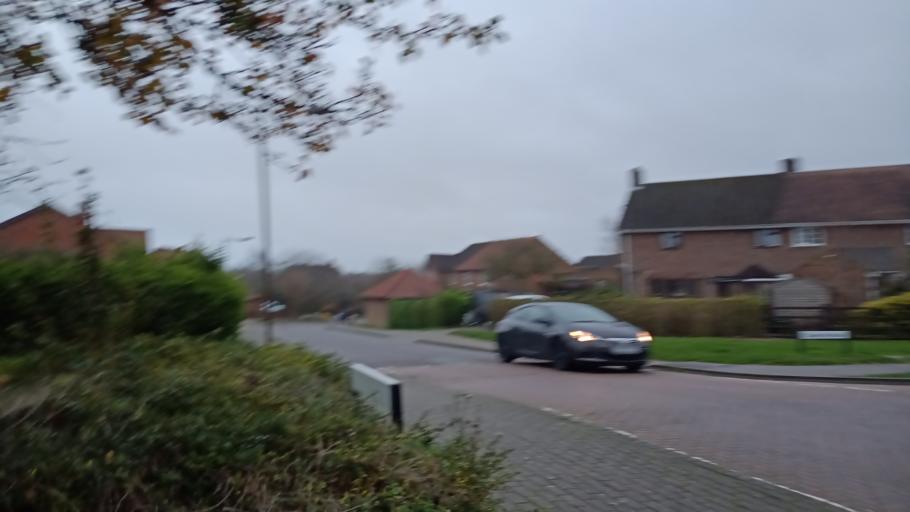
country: GB
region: England
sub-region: Milton Keynes
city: Shenley Church End
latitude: 52.0148
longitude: -0.7855
